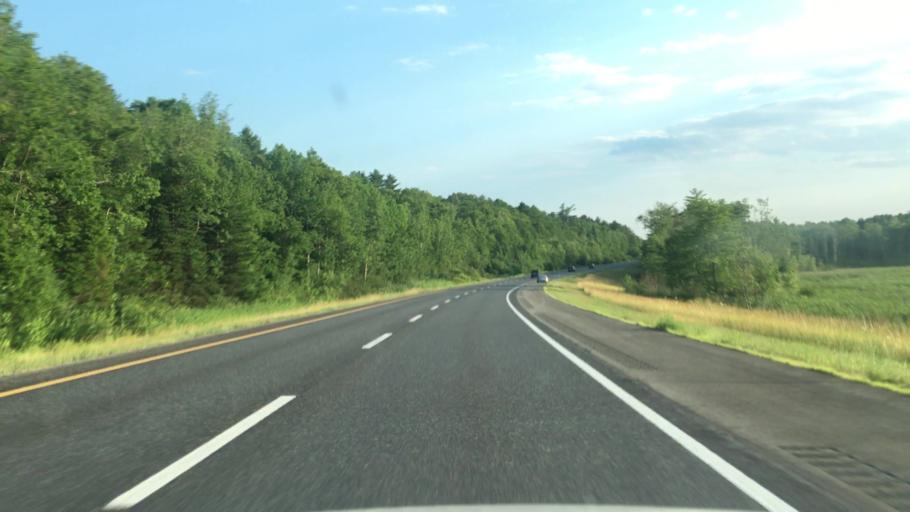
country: US
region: Maine
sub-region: Sagadahoc County
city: Topsham
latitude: 43.9763
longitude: -69.9468
